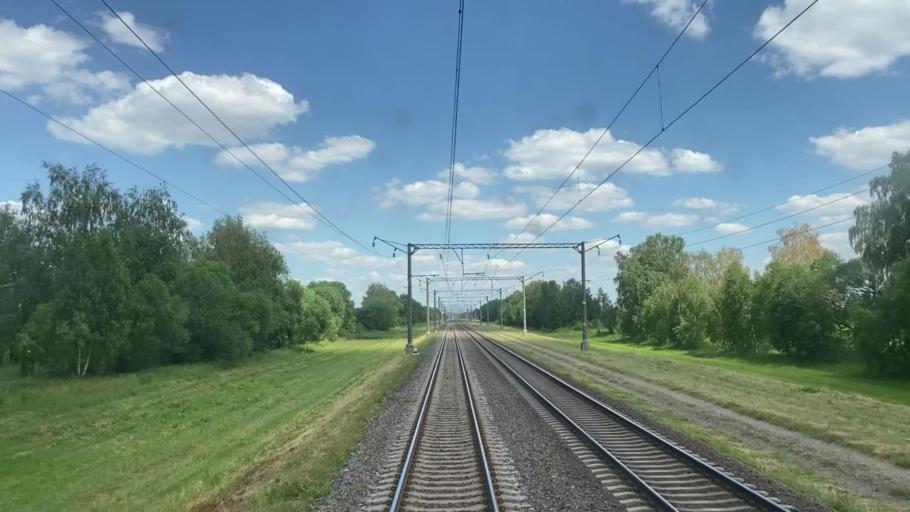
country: BY
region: Brest
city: Charnawchytsy
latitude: 52.1365
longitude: 23.8293
